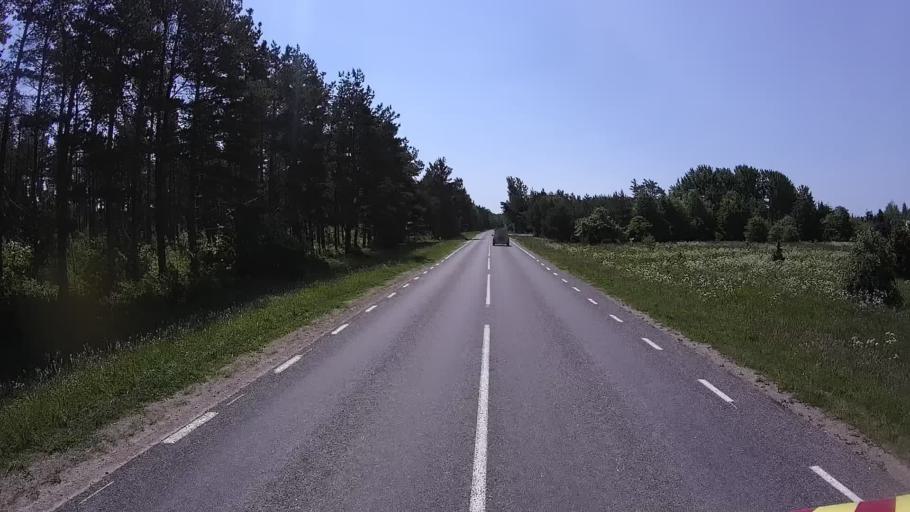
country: EE
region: Saare
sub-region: Kuressaare linn
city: Kuressaare
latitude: 58.1417
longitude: 22.2482
